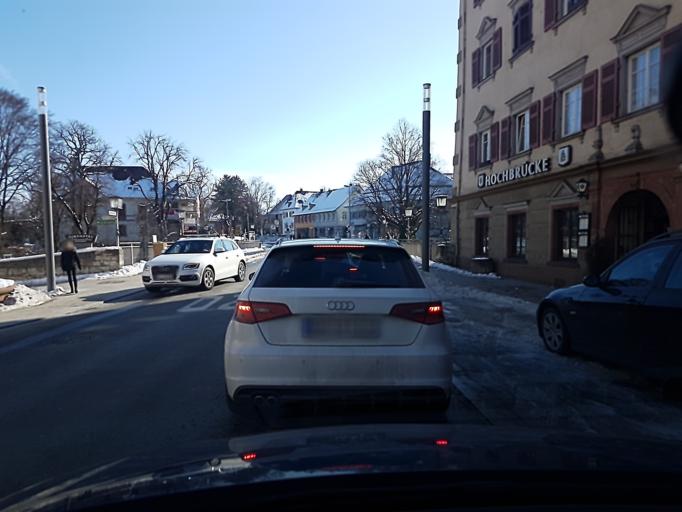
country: DE
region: Baden-Wuerttemberg
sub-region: Freiburg Region
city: Rottweil
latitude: 48.1665
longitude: 8.6280
